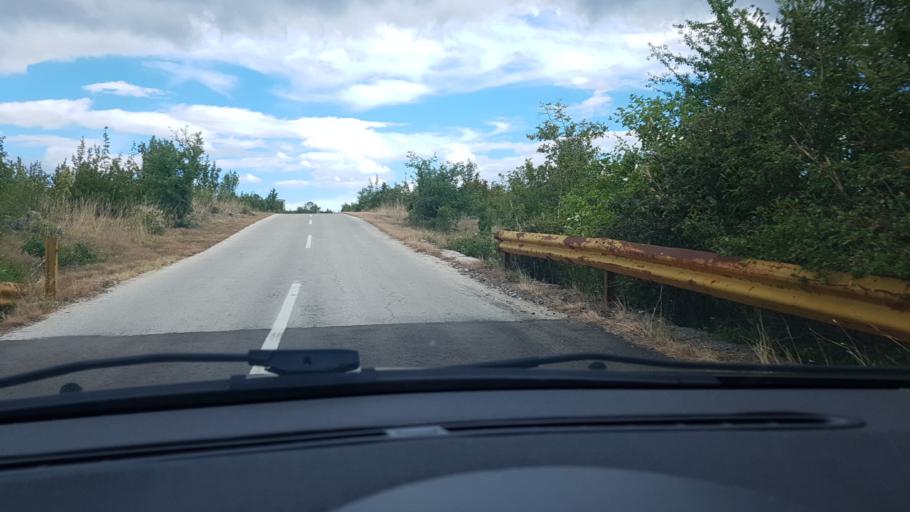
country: HR
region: Sibensko-Kniniska
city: Kistanje
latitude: 44.0906
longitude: 15.9387
